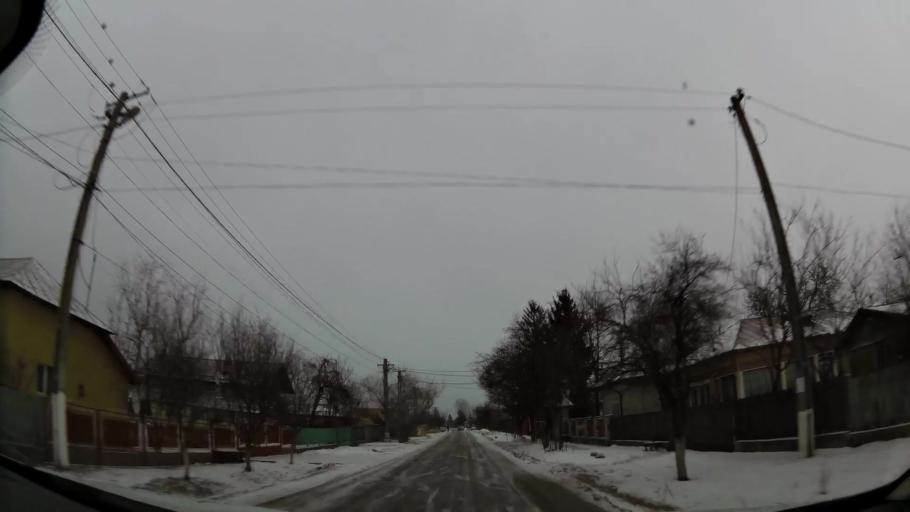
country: RO
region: Prahova
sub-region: Comuna Poenarii-Burchi
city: Ologeni
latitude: 44.7332
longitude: 25.9411
